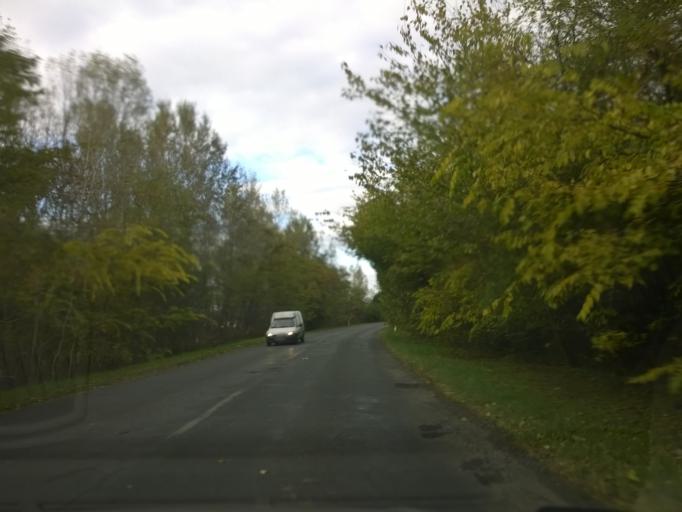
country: HU
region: Pest
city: Szigetujfalu
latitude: 47.2210
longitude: 18.9559
